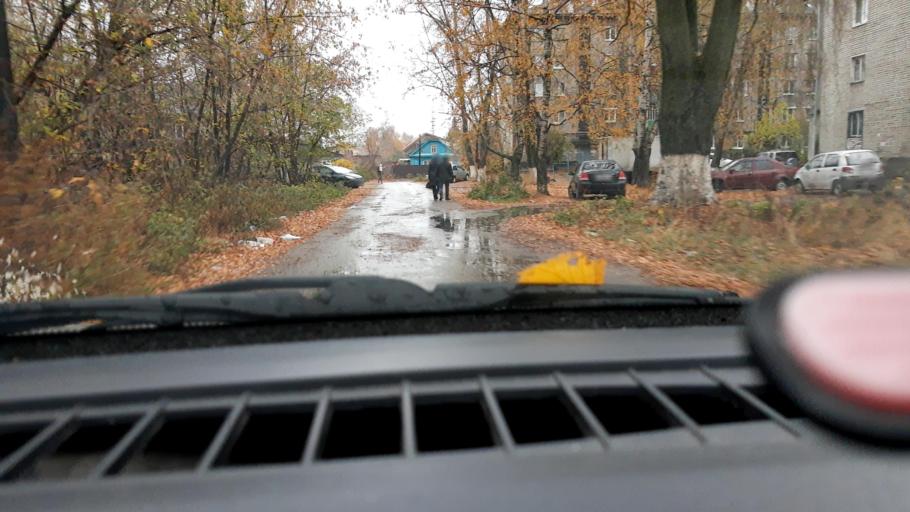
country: RU
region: Nizjnij Novgorod
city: Nizhniy Novgorod
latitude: 56.3020
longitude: 43.9117
